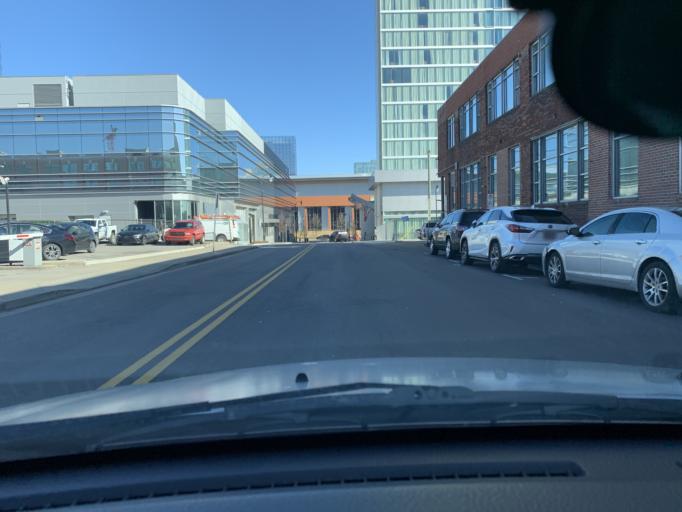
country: US
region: Tennessee
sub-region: Davidson County
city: Nashville
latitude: 36.1551
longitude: -86.7819
